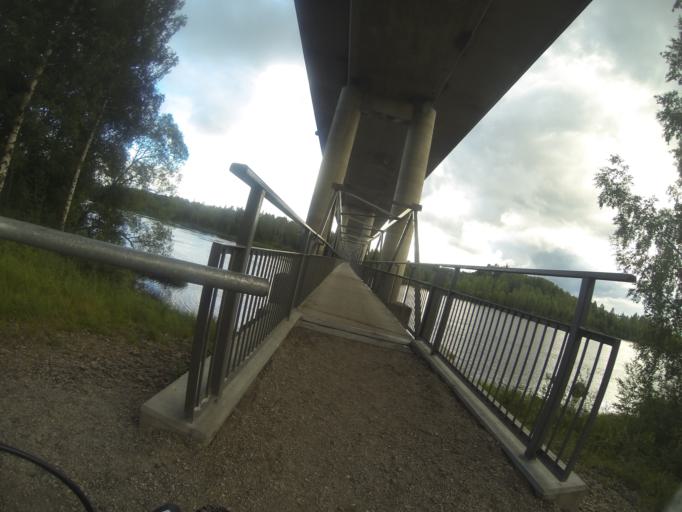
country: SE
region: Dalarna
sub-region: Avesta Kommun
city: Avesta
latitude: 60.1486
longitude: 16.2002
